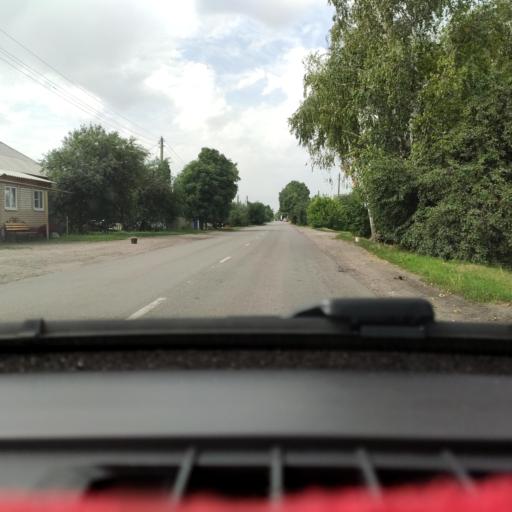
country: RU
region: Voronezj
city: Davydovka
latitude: 51.2060
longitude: 39.5127
